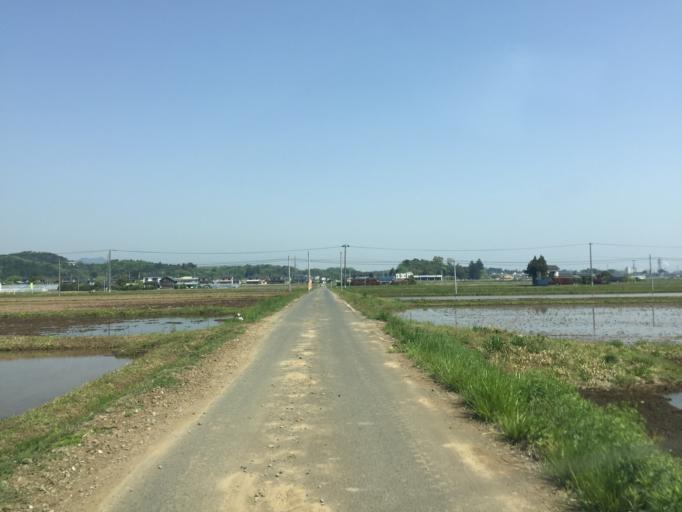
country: JP
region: Miyagi
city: Marumori
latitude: 37.7798
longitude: 140.9107
